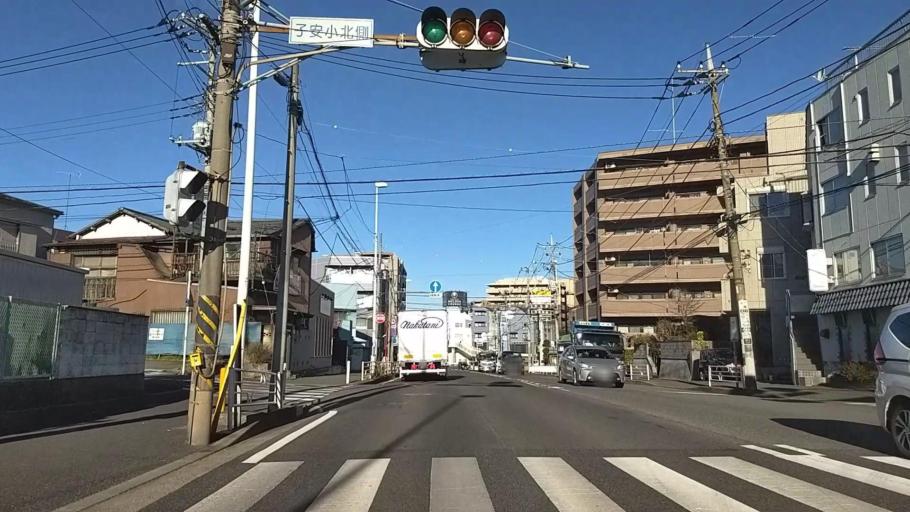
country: JP
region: Kanagawa
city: Yokohama
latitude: 35.4888
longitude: 139.6532
